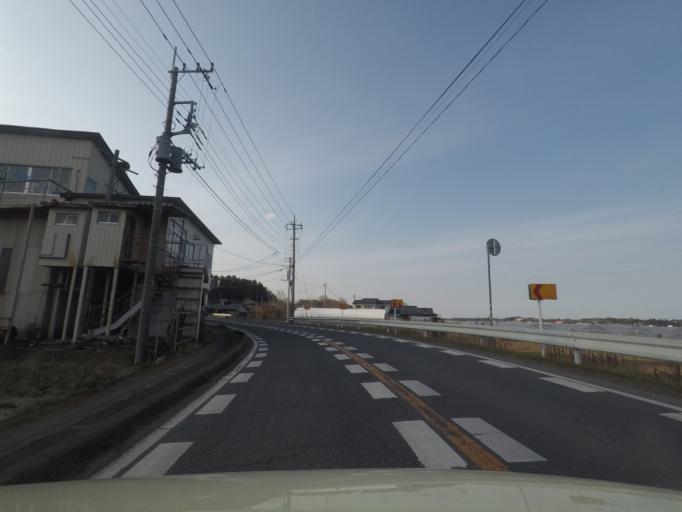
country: JP
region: Ibaraki
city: Okunoya
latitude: 36.2720
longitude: 140.4376
